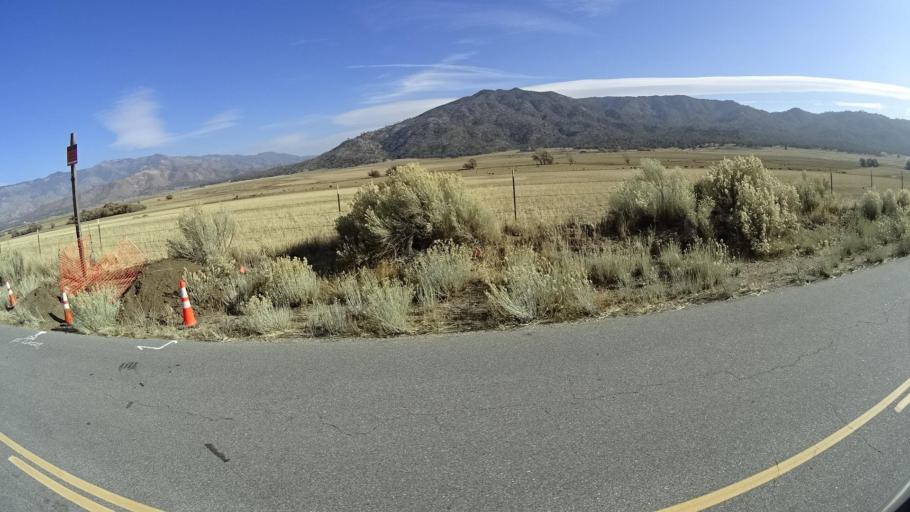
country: US
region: California
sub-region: Kern County
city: Bodfish
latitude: 35.3985
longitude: -118.5471
